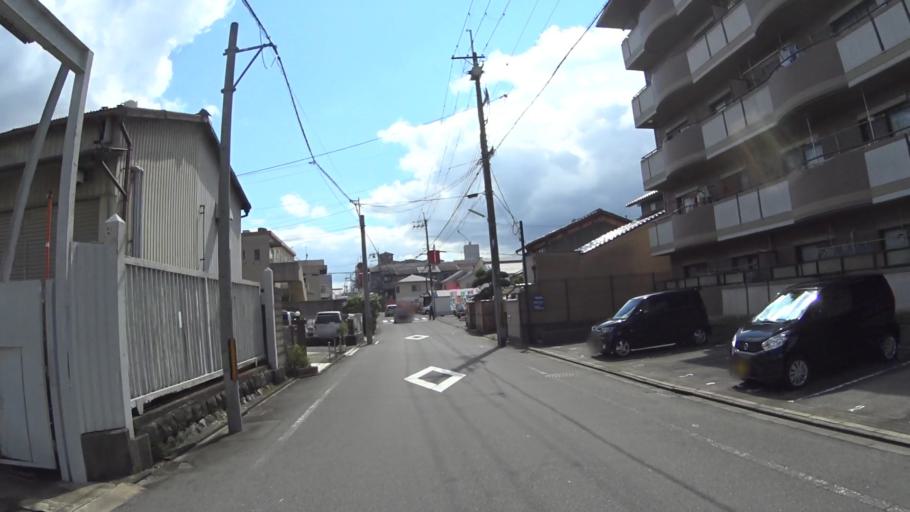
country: JP
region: Kyoto
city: Muko
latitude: 34.9380
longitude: 135.7576
